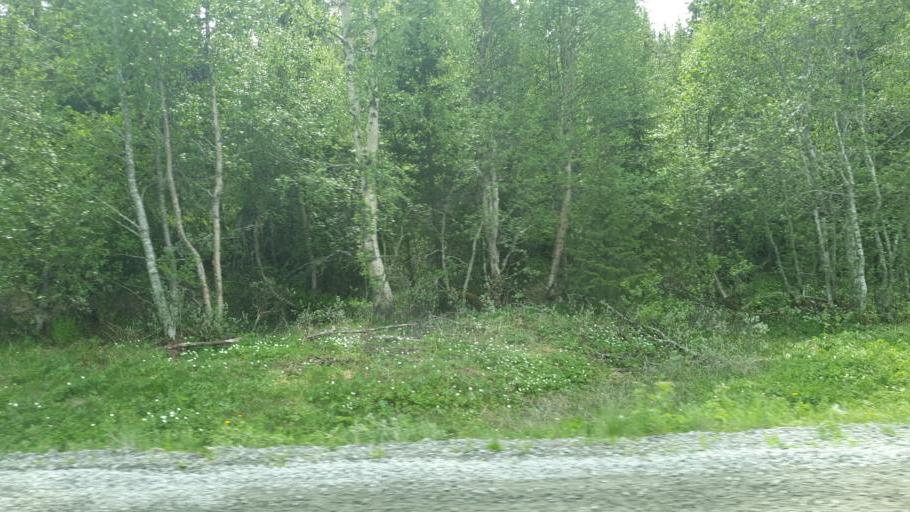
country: NO
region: Nord-Trondelag
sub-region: Leksvik
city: Leksvik
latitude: 63.6974
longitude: 10.4911
